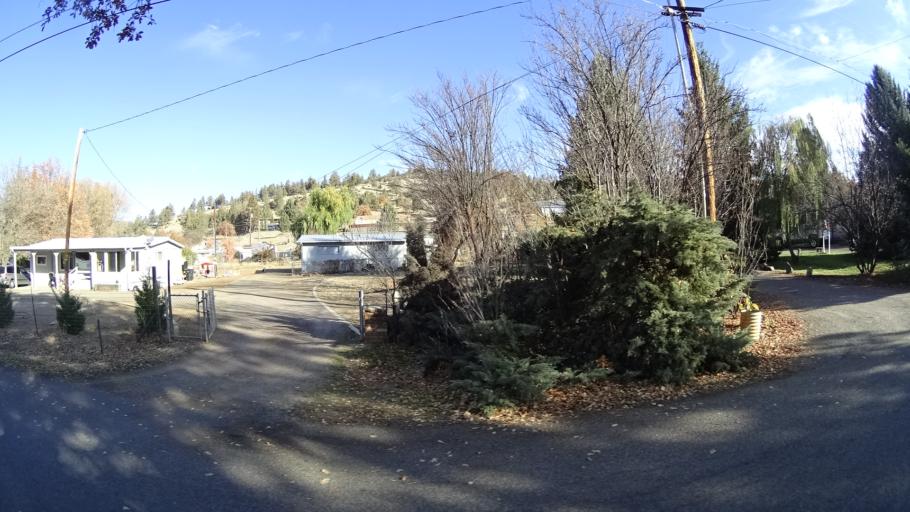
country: US
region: California
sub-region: Siskiyou County
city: Yreka
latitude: 41.6987
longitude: -122.6360
